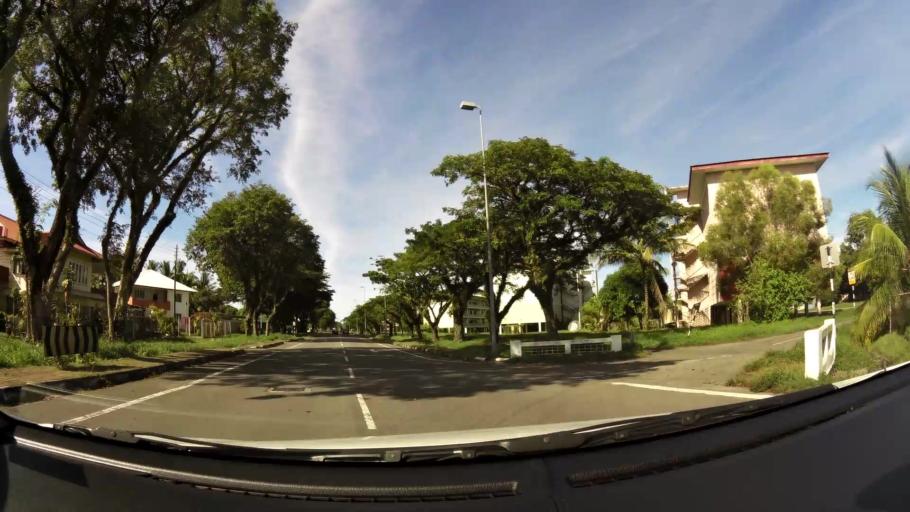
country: BN
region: Belait
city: Kuala Belait
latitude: 4.5793
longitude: 114.1988
